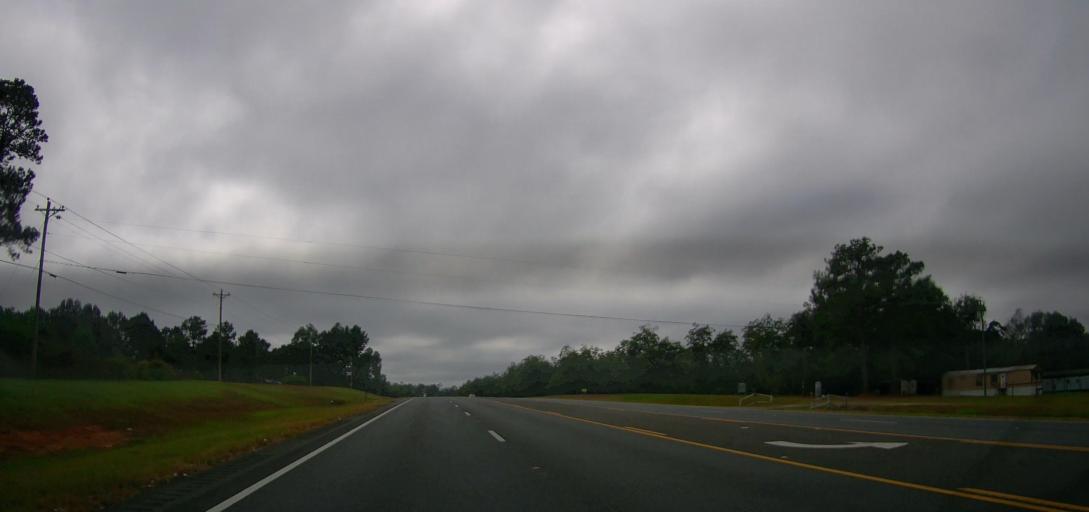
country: US
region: Georgia
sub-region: Thomas County
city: Thomasville
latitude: 30.9573
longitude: -83.8955
